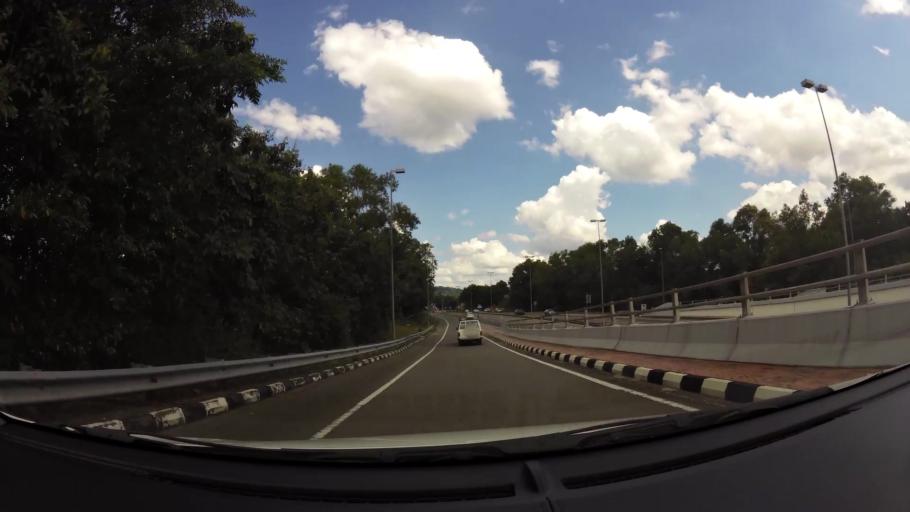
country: BN
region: Brunei and Muara
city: Bandar Seri Begawan
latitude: 4.9485
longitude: 114.9649
